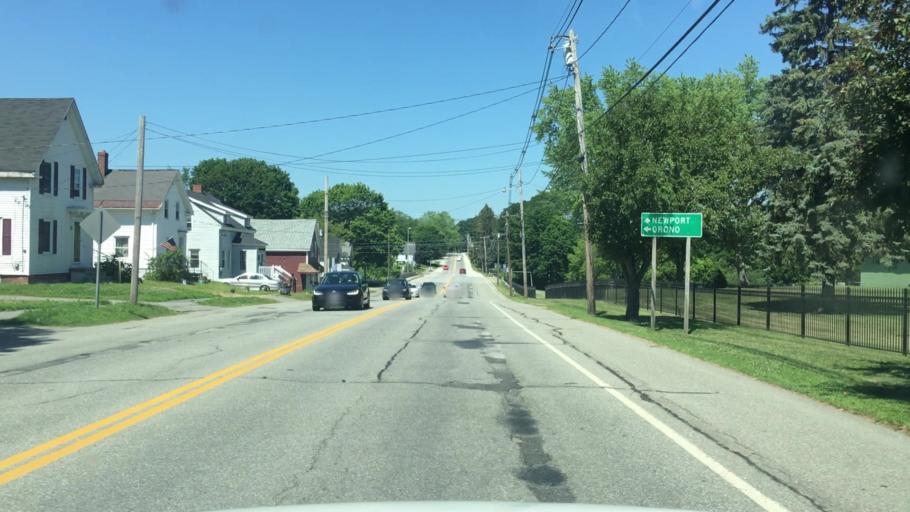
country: US
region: Maine
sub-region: Penobscot County
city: Bangor
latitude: 44.8107
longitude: -68.7888
